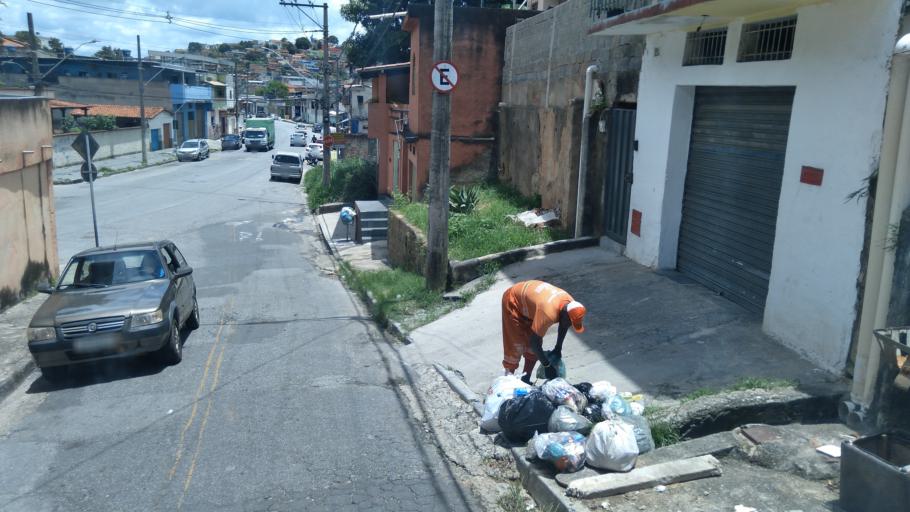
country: BR
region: Minas Gerais
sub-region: Belo Horizonte
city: Belo Horizonte
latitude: -19.8538
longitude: -43.8992
